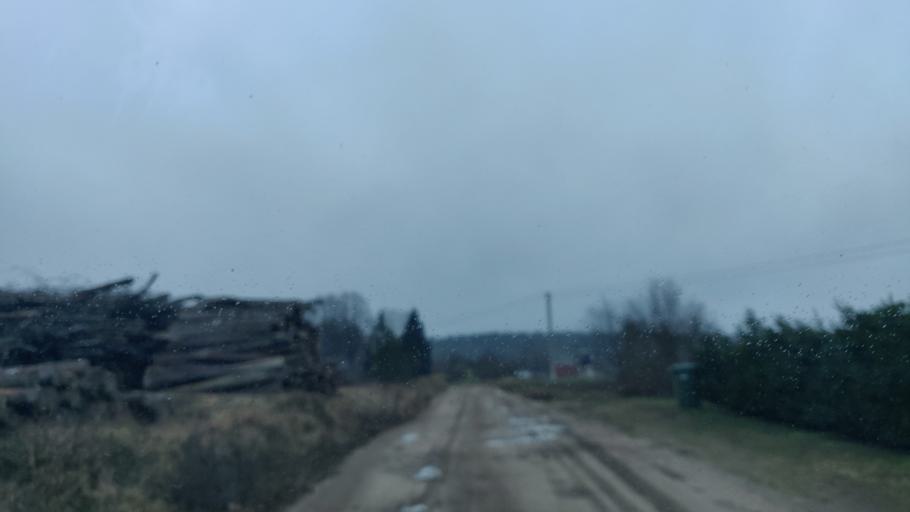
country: LT
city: Trakai
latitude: 54.5594
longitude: 24.9327
